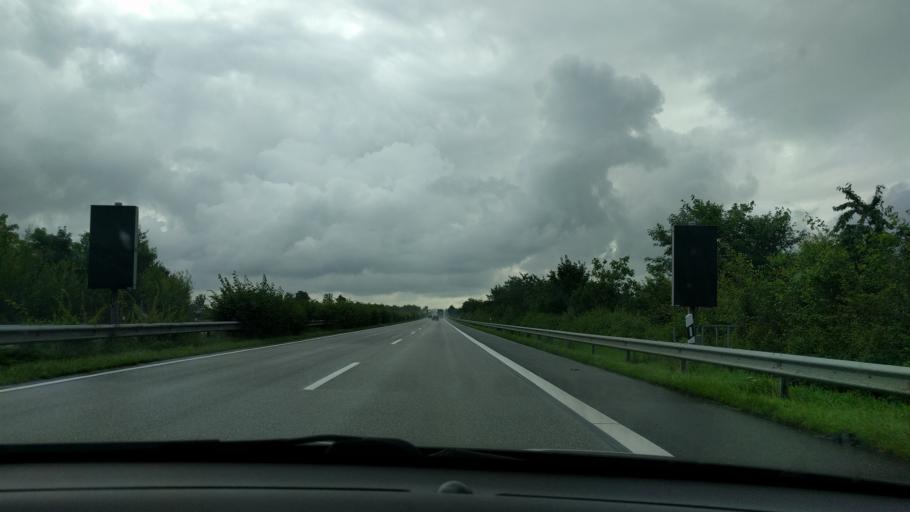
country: DE
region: Schleswig-Holstein
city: Schafstedt
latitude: 54.0738
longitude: 9.2911
